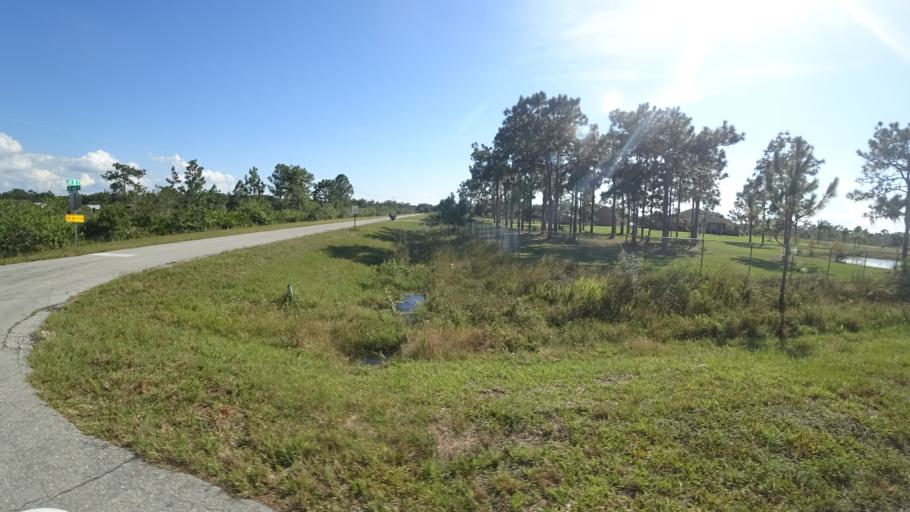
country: US
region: Florida
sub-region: Sarasota County
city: The Meadows
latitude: 27.4160
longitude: -82.2753
